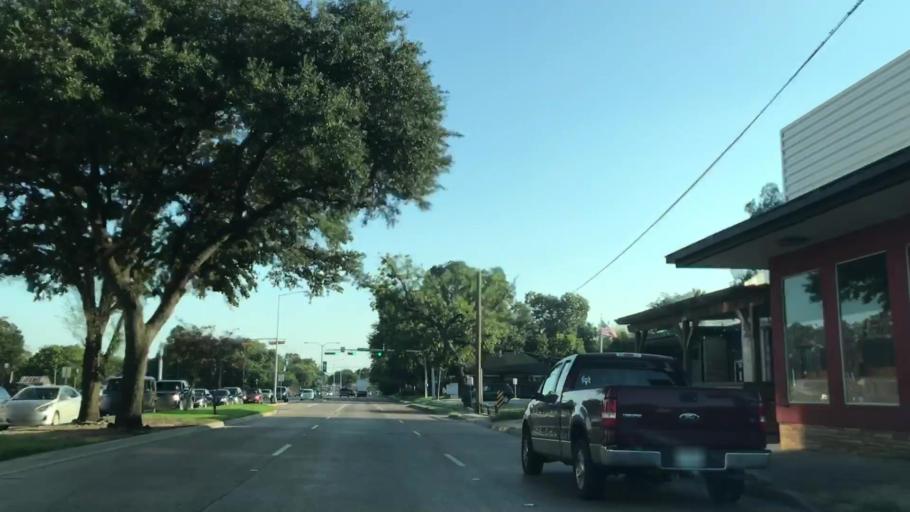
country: US
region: Texas
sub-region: Denton County
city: Denton
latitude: 33.2145
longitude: -97.1371
